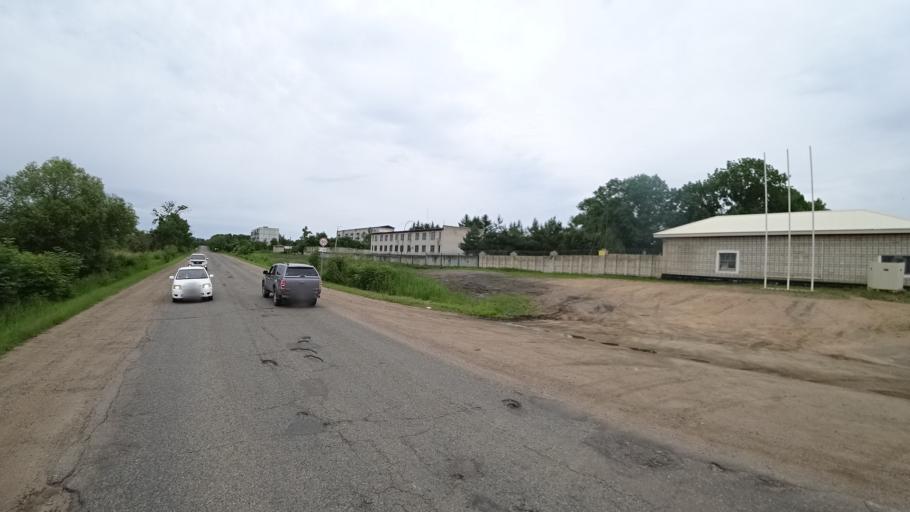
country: RU
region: Primorskiy
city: Novosysoyevka
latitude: 44.1803
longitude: 133.3490
